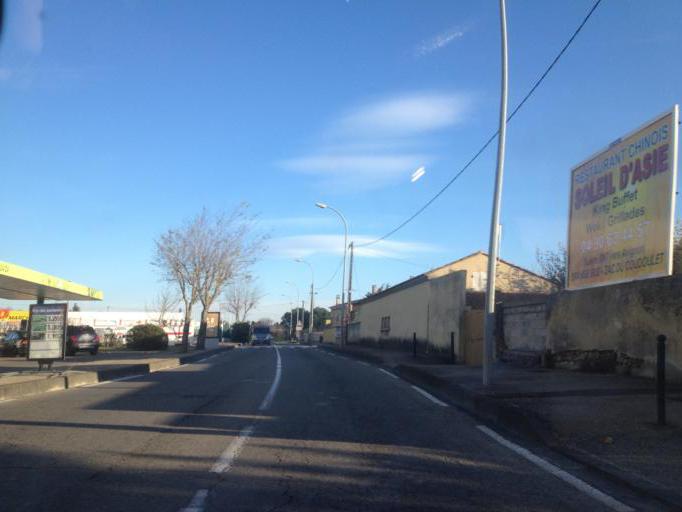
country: FR
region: Provence-Alpes-Cote d'Azur
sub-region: Departement du Vaucluse
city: Orange
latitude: 44.1520
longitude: 4.8038
